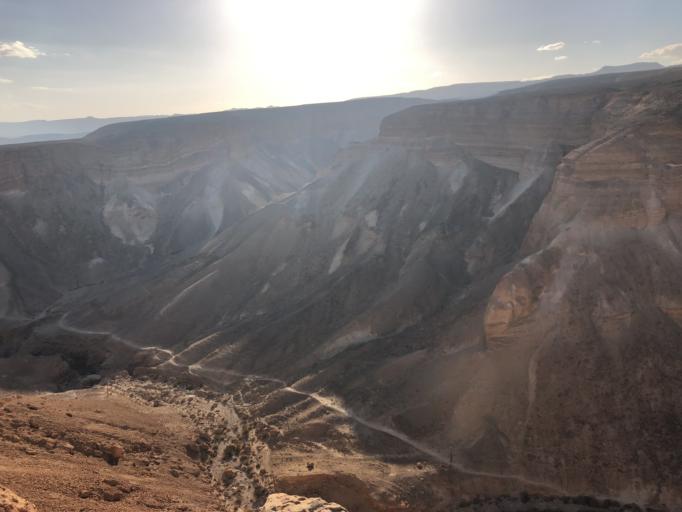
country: IL
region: Southern District
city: `En Boqeq
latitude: 31.3141
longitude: 35.3525
